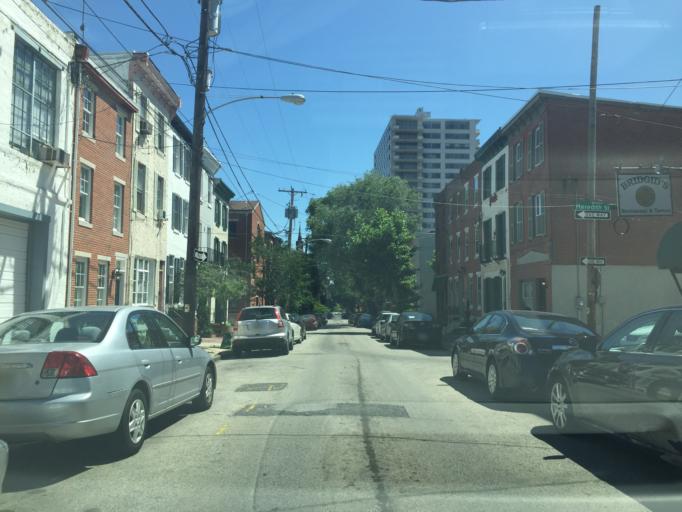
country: US
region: Pennsylvania
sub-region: Philadelphia County
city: Philadelphia
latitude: 39.9687
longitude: -75.1767
